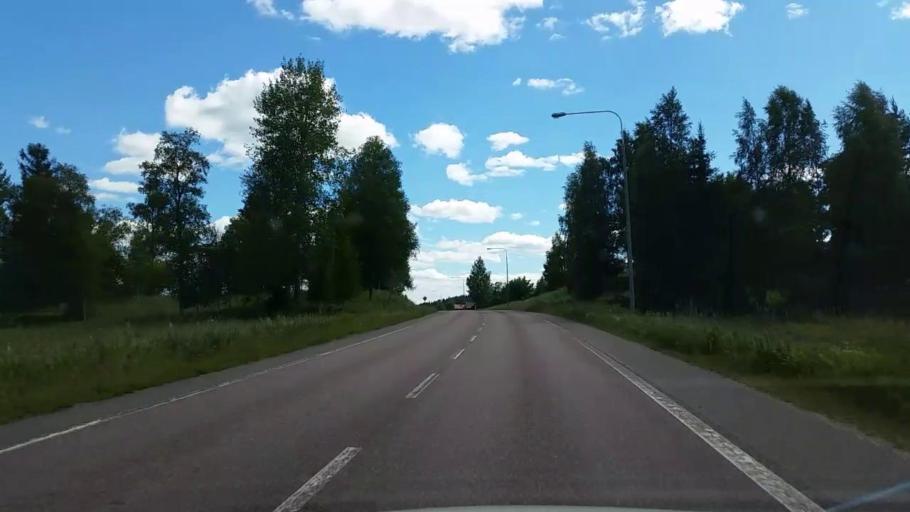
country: SE
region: Dalarna
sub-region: Faluns Kommun
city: Svardsjo
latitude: 60.8587
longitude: 15.7494
